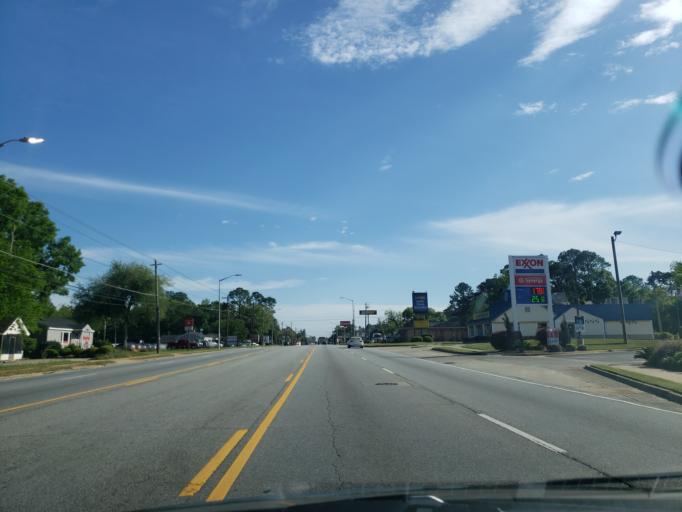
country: US
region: Georgia
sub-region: Dougherty County
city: Albany
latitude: 31.6020
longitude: -84.1759
